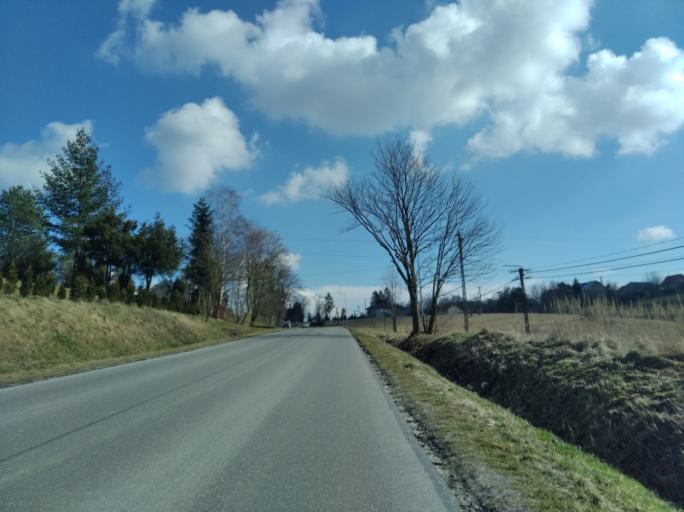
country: PL
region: Subcarpathian Voivodeship
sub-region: Powiat strzyzowski
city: Frysztak
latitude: 49.8491
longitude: 21.5223
